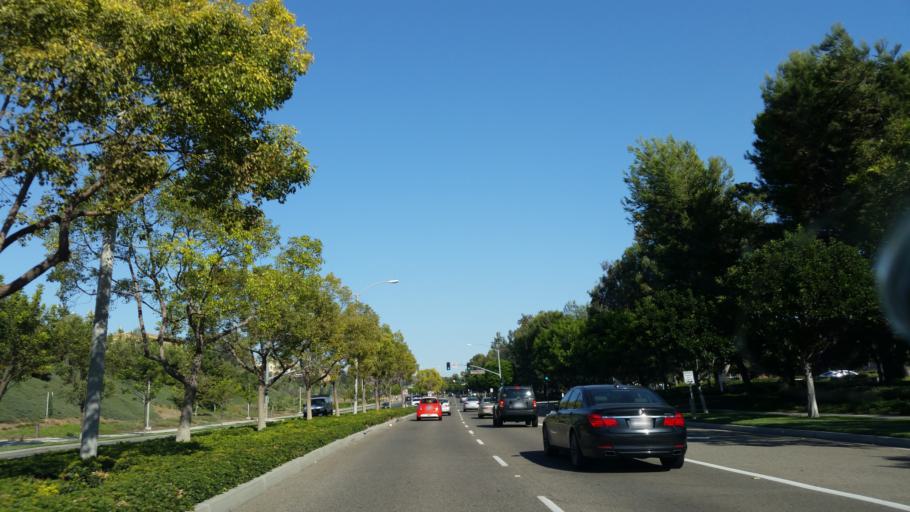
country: US
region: California
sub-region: Orange County
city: San Joaquin Hills
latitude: 33.6335
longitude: -117.8343
